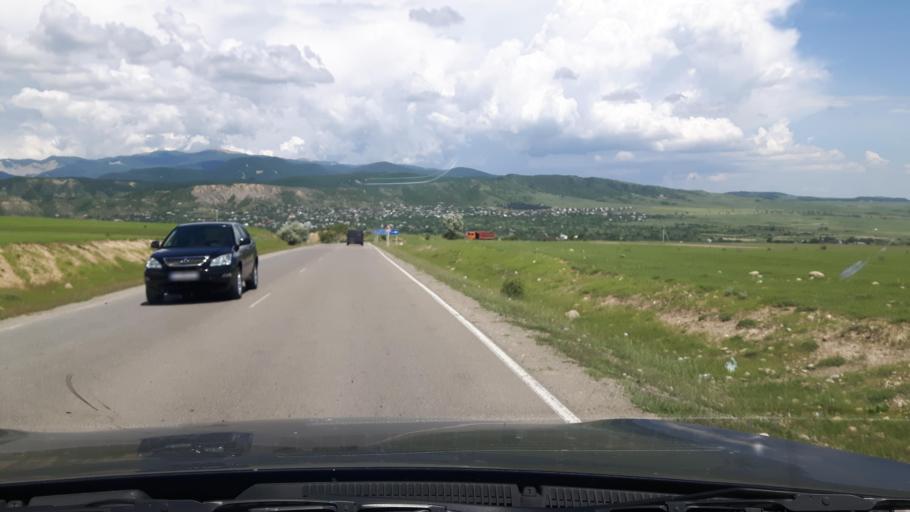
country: GE
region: Kakheti
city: Sagarejo
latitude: 41.7534
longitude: 45.1496
